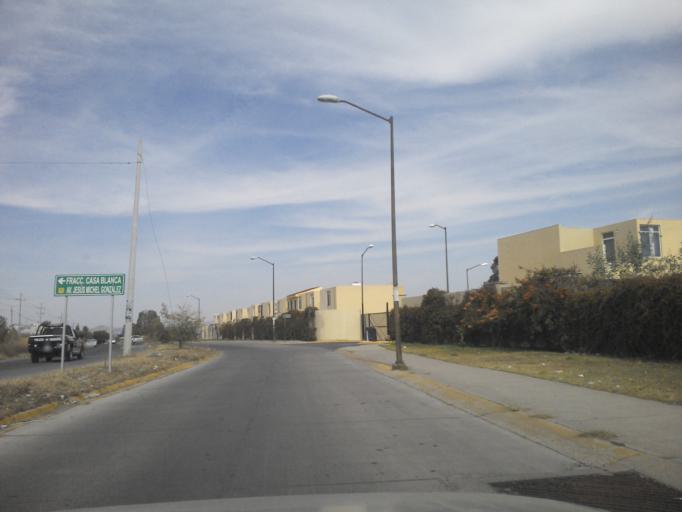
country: MX
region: Jalisco
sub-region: Tlajomulco de Zuniga
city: Lomas del Sur
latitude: 20.4998
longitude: -103.4156
